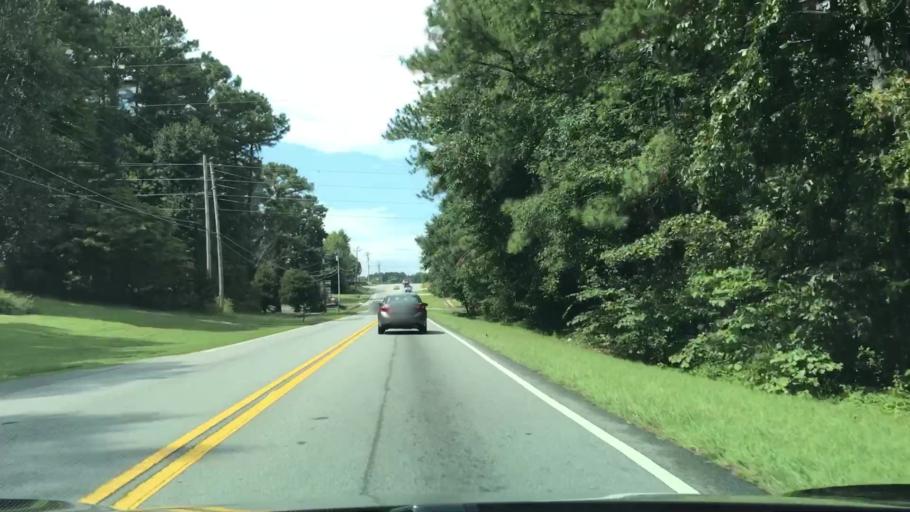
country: US
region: Georgia
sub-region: Gwinnett County
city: Snellville
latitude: 33.8832
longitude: -84.0577
